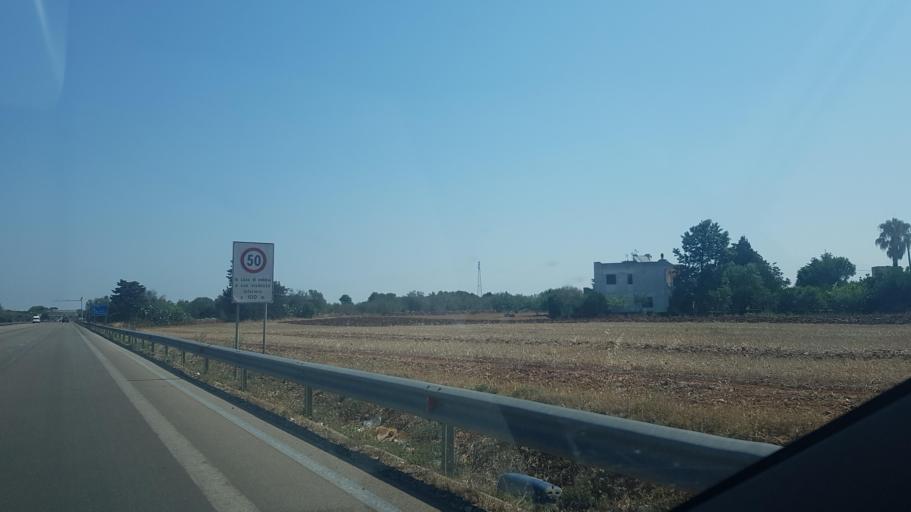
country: IT
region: Apulia
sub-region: Provincia di Lecce
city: Scorrano
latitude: 40.0897
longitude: 18.3106
